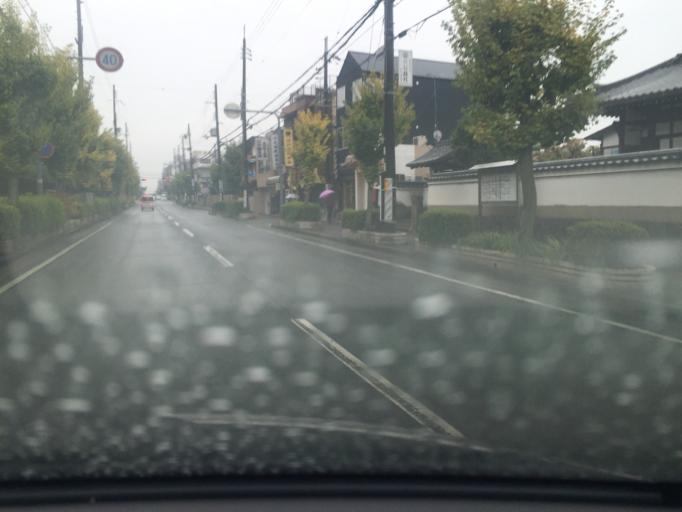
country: JP
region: Nara
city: Nara-shi
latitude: 34.6881
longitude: 135.8261
